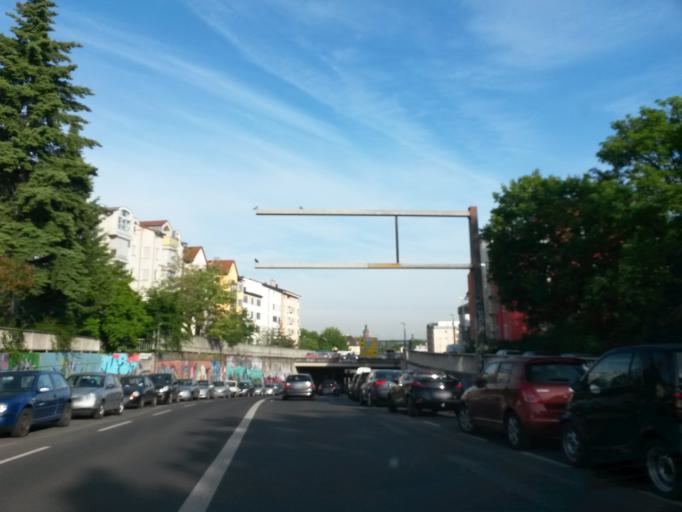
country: DE
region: Bavaria
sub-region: Regierungsbezirk Unterfranken
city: Wuerzburg
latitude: 49.7862
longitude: 9.9448
